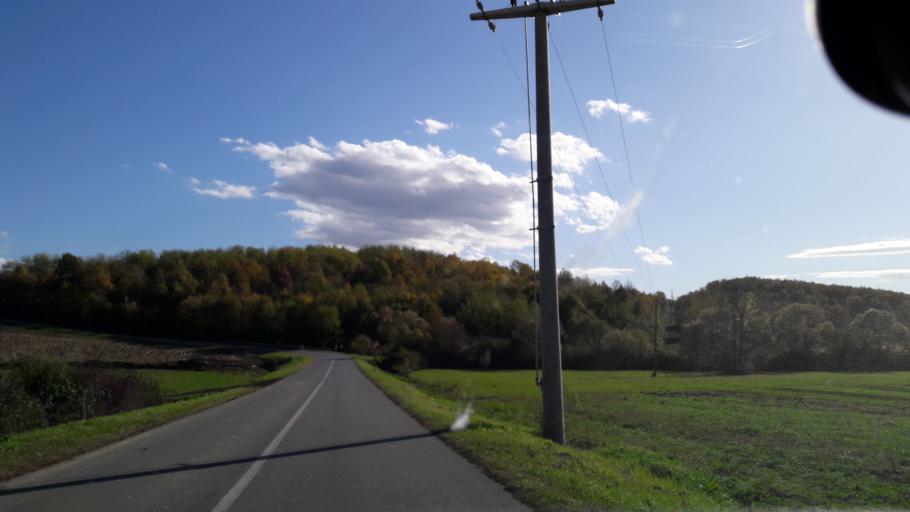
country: HR
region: Osjecko-Baranjska
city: Vukojevci
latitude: 45.3904
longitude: 18.2437
